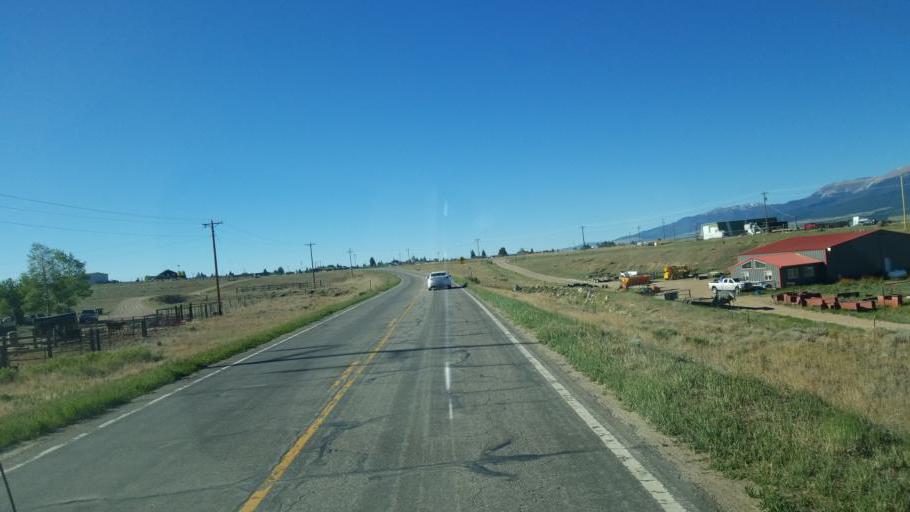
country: US
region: Colorado
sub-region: Custer County
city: Westcliffe
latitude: 38.1457
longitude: -105.4754
